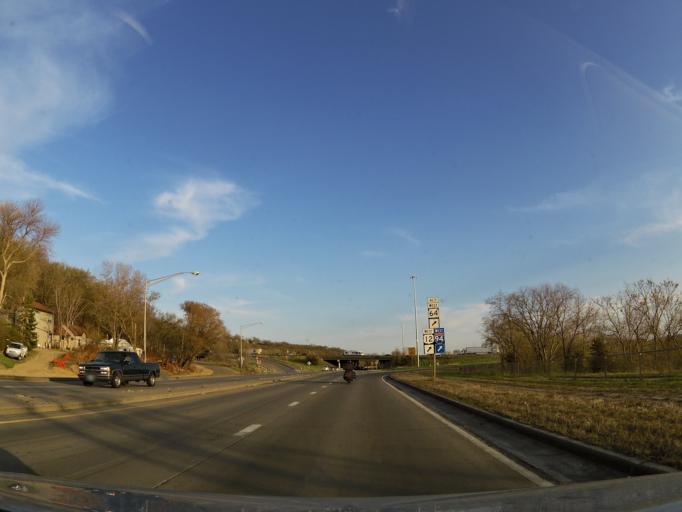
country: US
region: Wisconsin
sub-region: Saint Croix County
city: Hudson
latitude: 44.9649
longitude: -92.7542
